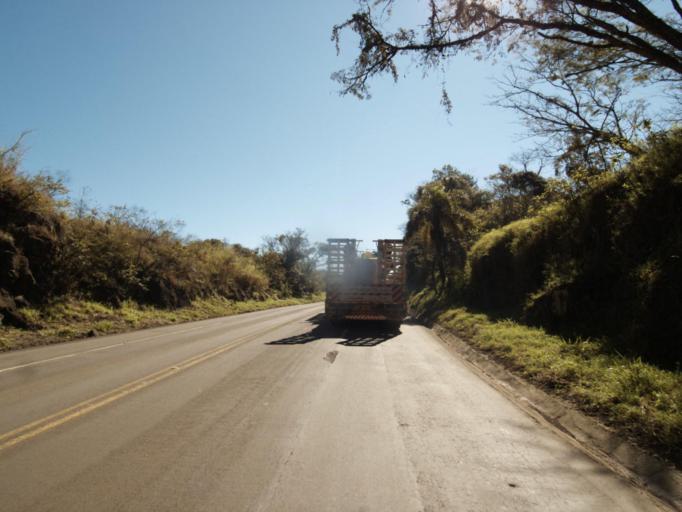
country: BR
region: Rio Grande do Sul
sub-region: Frederico Westphalen
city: Frederico Westphalen
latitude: -26.8196
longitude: -53.4276
